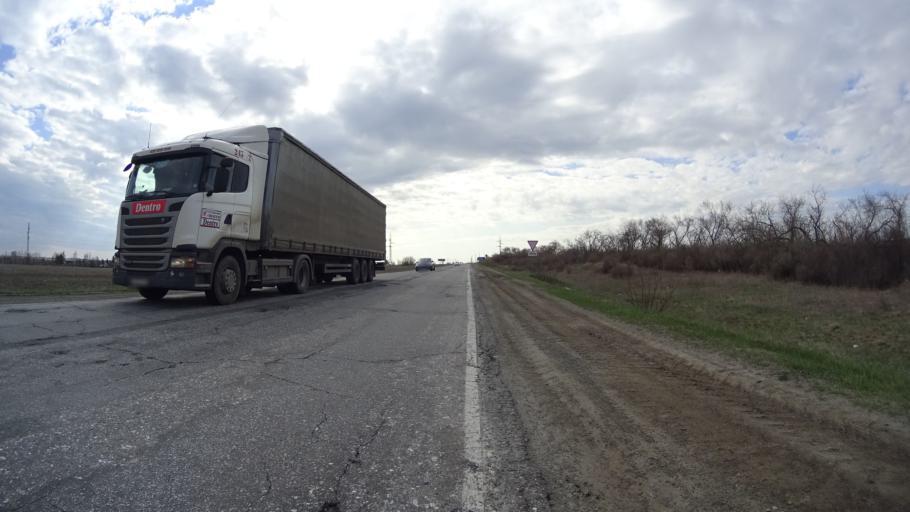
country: RU
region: Chelyabinsk
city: Troitsk
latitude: 54.0949
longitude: 61.4781
